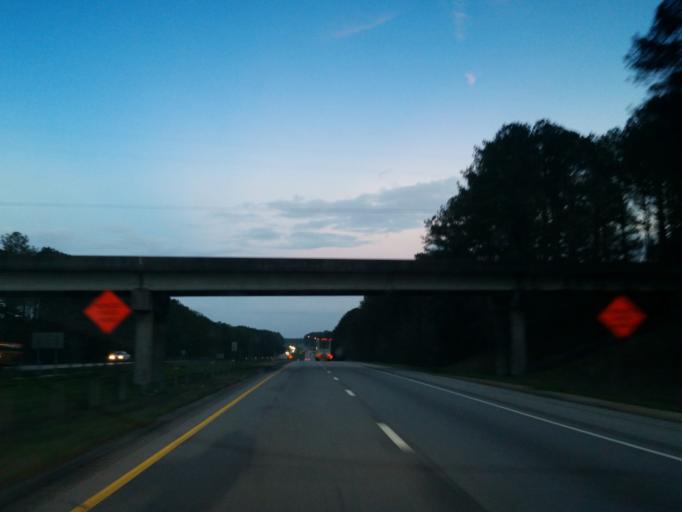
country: US
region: Alabama
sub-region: Sumter County
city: York
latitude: 32.4451
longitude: -88.4157
